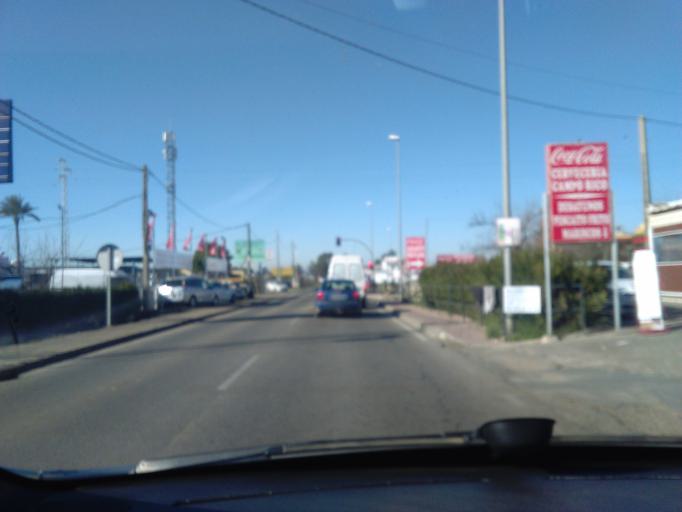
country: ES
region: Andalusia
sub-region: Provincia de Sevilla
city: Sevilla
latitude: 37.4263
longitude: -5.9289
